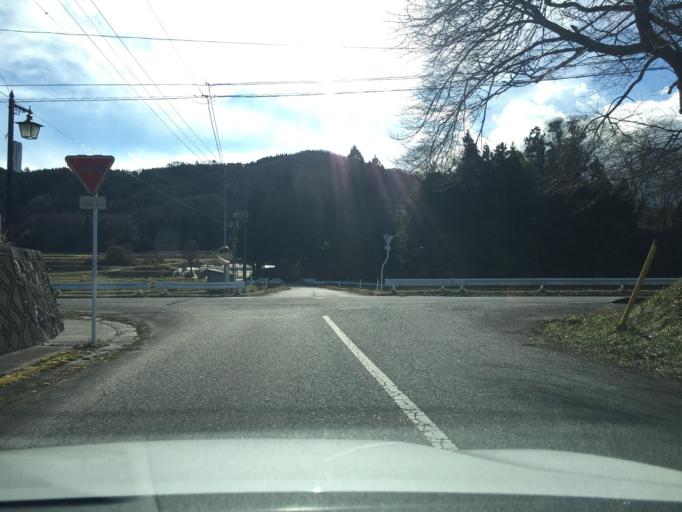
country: JP
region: Fukushima
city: Funehikimachi-funehiki
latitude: 37.3590
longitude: 140.6174
